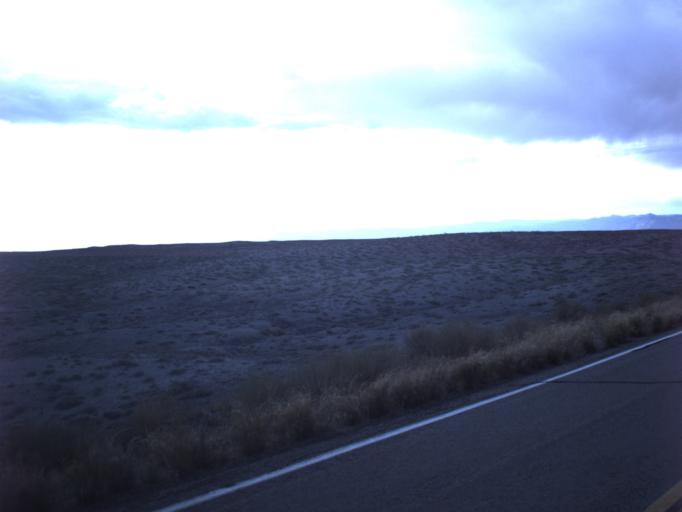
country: US
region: Utah
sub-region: Grand County
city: Moab
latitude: 38.8953
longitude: -109.3112
